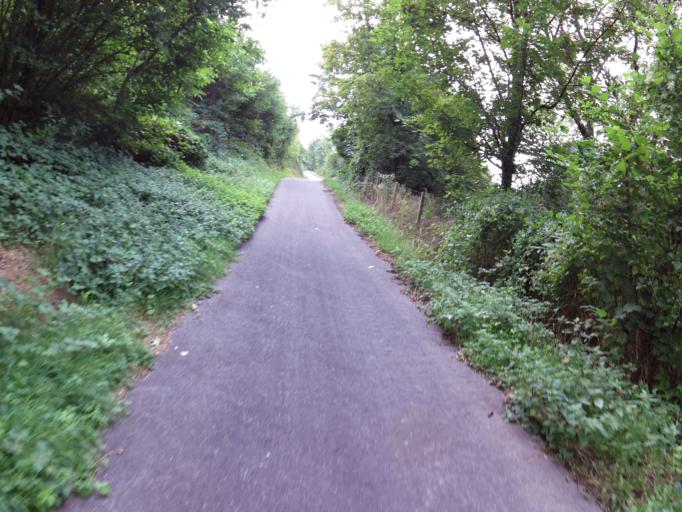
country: DE
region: Rheinland-Pfalz
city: Metterich
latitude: 49.9780
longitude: 6.5814
